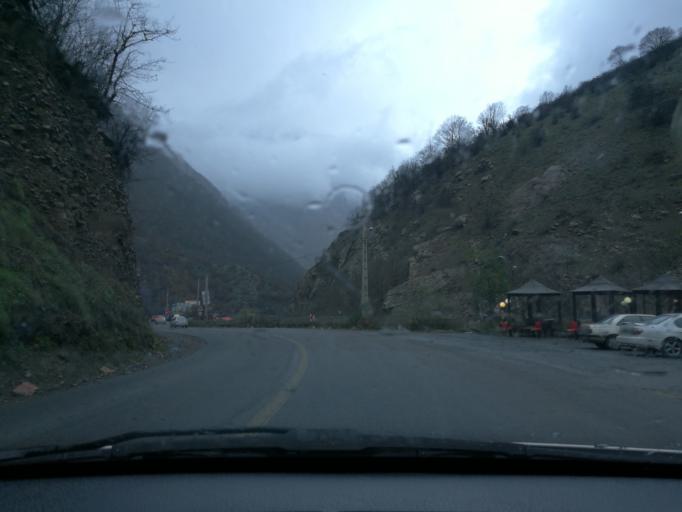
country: IR
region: Mazandaran
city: Chalus
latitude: 36.2645
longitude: 51.2606
